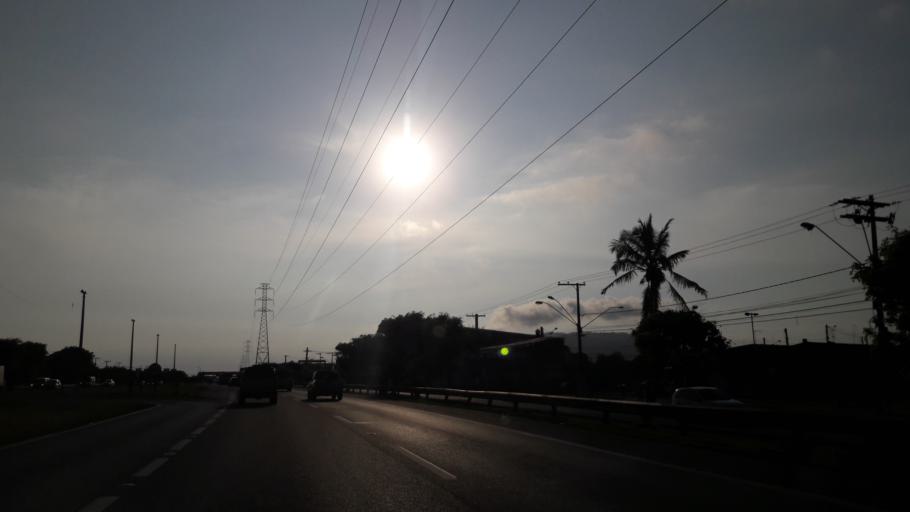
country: BR
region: Sao Paulo
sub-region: Mongagua
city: Mongagua
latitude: -24.1298
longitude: -46.6925
